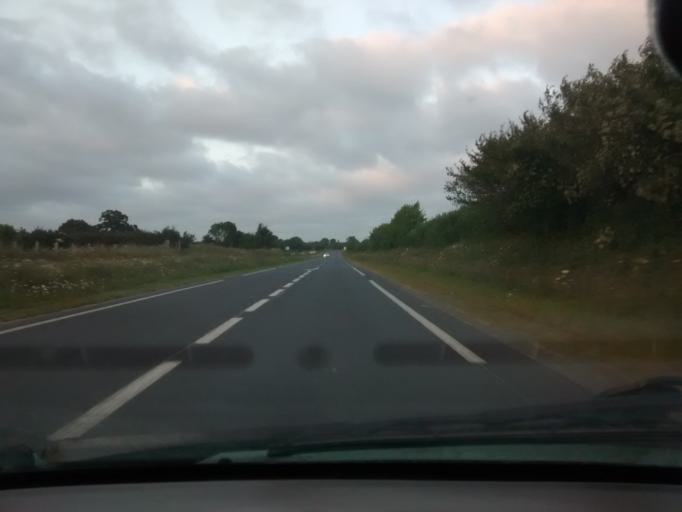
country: FR
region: Lower Normandy
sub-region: Departement de la Manche
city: Agneaux
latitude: 49.0985
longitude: -1.1041
